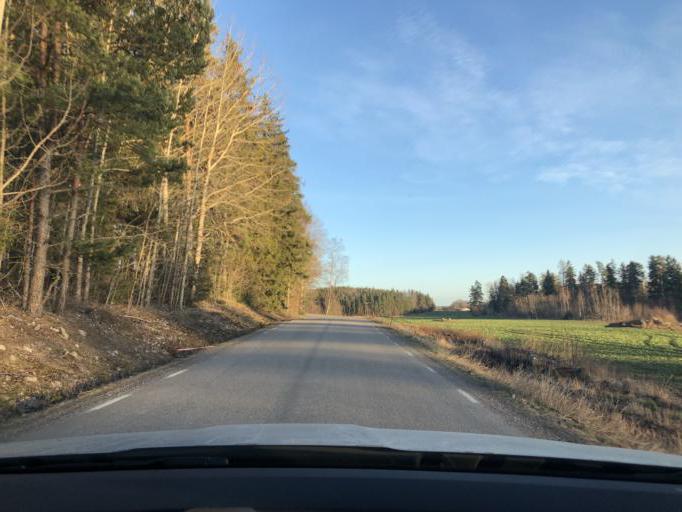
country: SE
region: Soedermanland
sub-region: Eskilstuna Kommun
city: Arla
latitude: 59.4190
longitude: 16.6638
